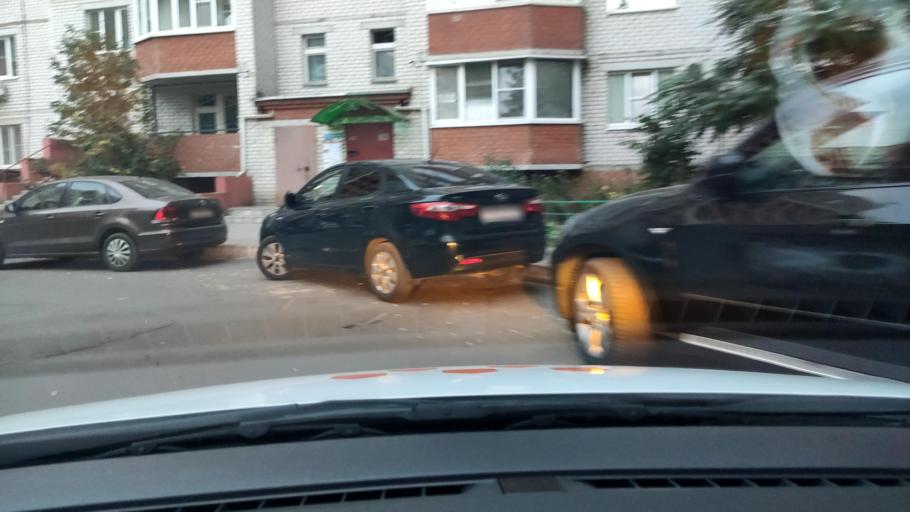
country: RU
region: Voronezj
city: Podgornoye
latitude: 51.7100
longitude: 39.1434
